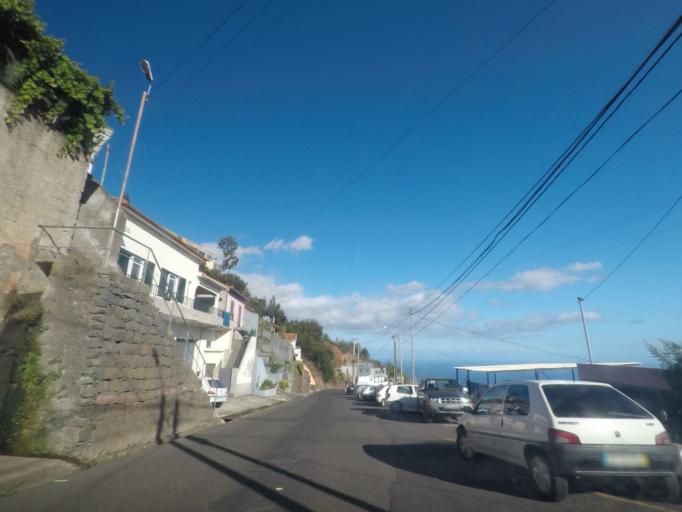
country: PT
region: Madeira
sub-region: Ribeira Brava
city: Campanario
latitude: 32.6654
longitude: -16.9972
